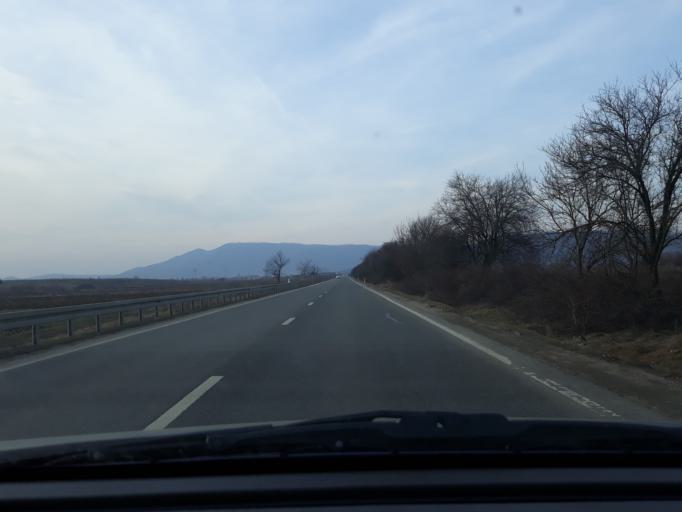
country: RO
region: Salaj
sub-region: Comuna Periceiu
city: Periceiu
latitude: 47.2156
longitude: 22.8968
